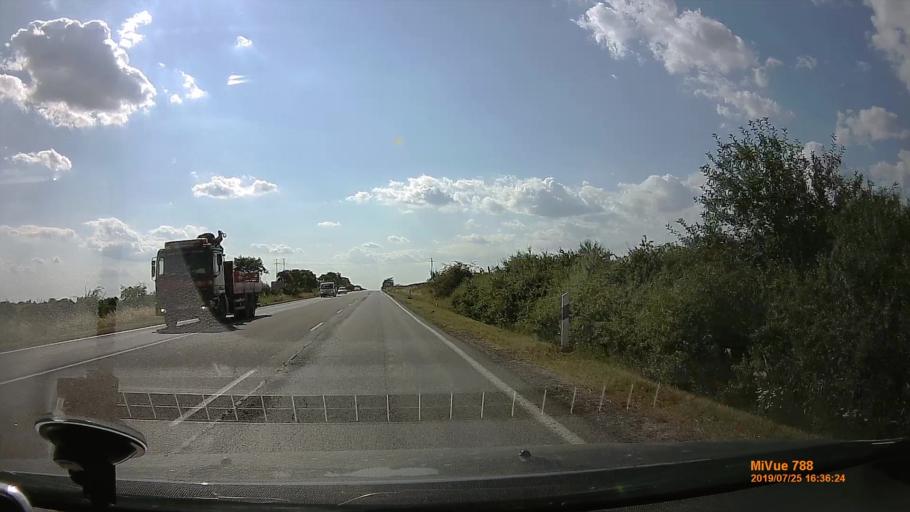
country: HU
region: Heves
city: Abasar
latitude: 47.7691
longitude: 19.9827
